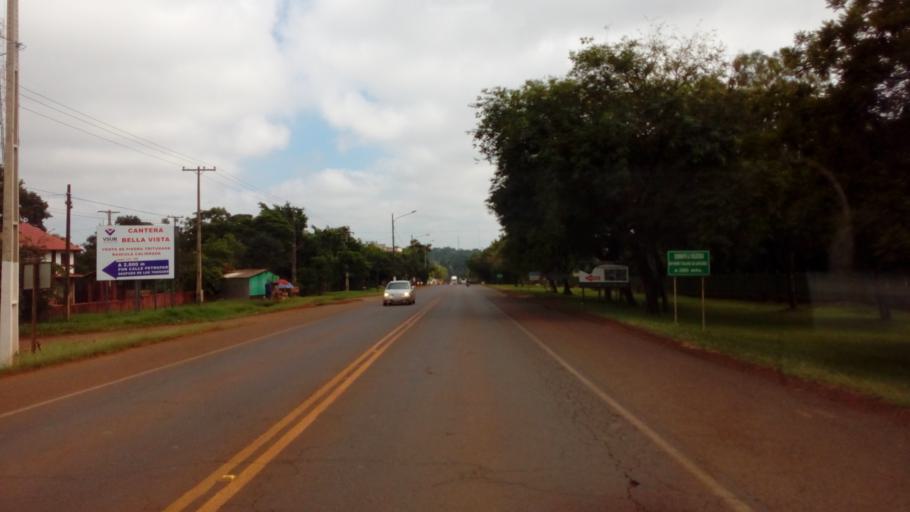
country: PY
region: Alto Parana
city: Ciudad del Este
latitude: -25.4235
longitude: -54.6374
